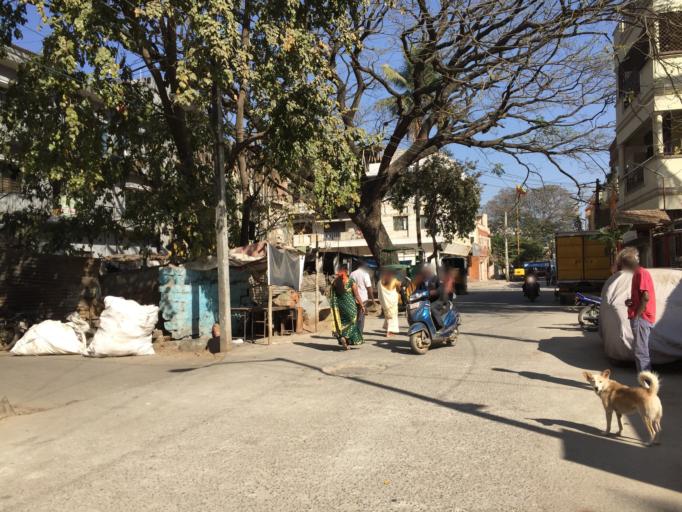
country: IN
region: Karnataka
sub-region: Bangalore Urban
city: Bangalore
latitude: 12.9584
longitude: 77.5920
